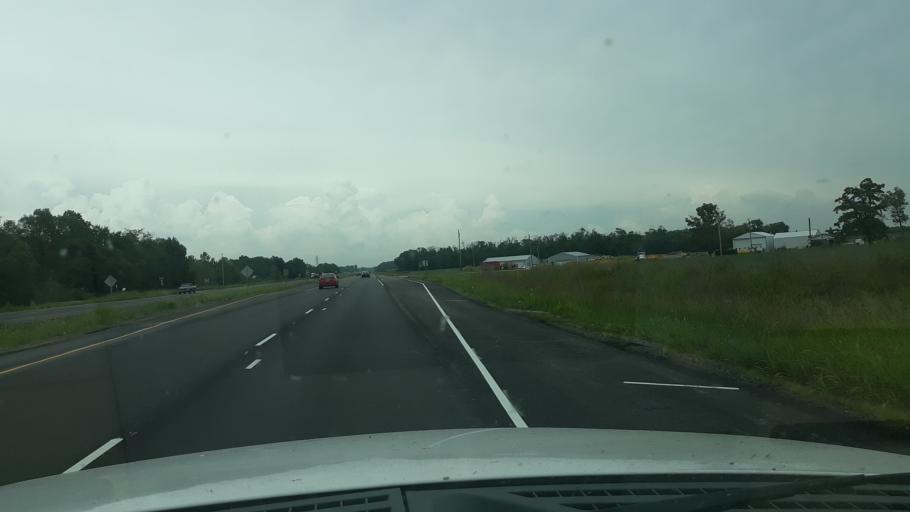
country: US
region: Illinois
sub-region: Saline County
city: Harrisburg
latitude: 37.7702
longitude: -88.5099
